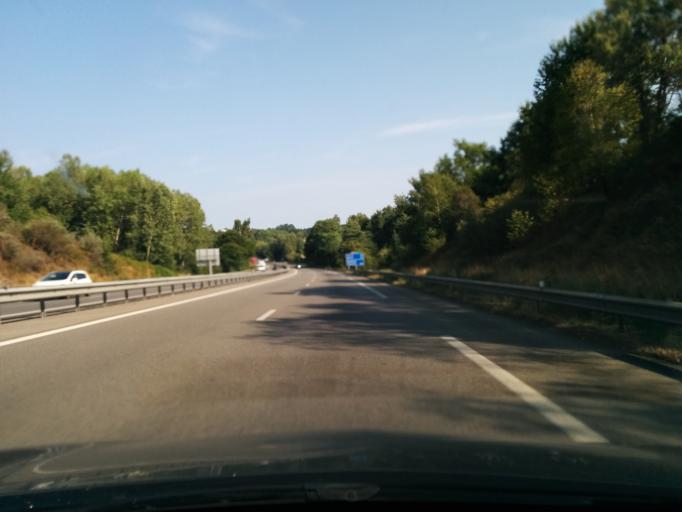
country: FR
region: Limousin
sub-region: Departement de la Haute-Vienne
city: Boisseuil
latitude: 45.7737
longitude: 1.3104
